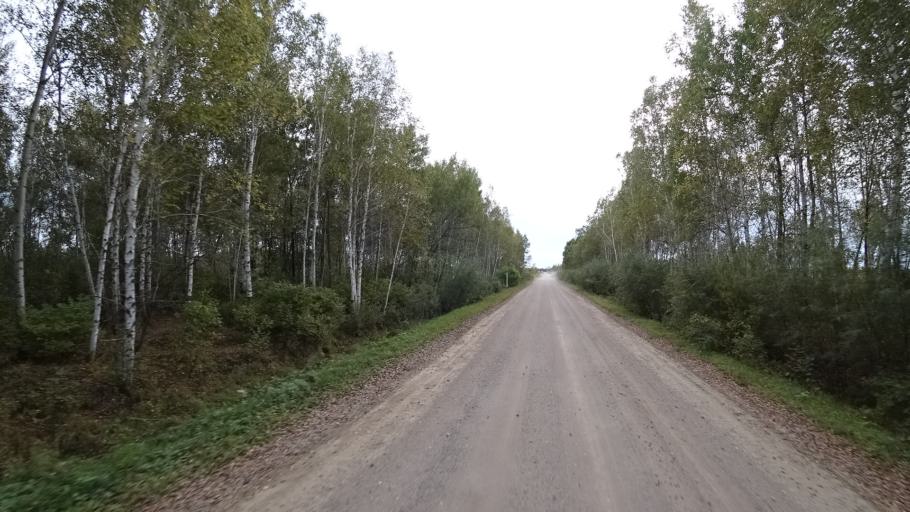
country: RU
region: Amur
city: Arkhara
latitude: 49.3799
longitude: 130.2149
